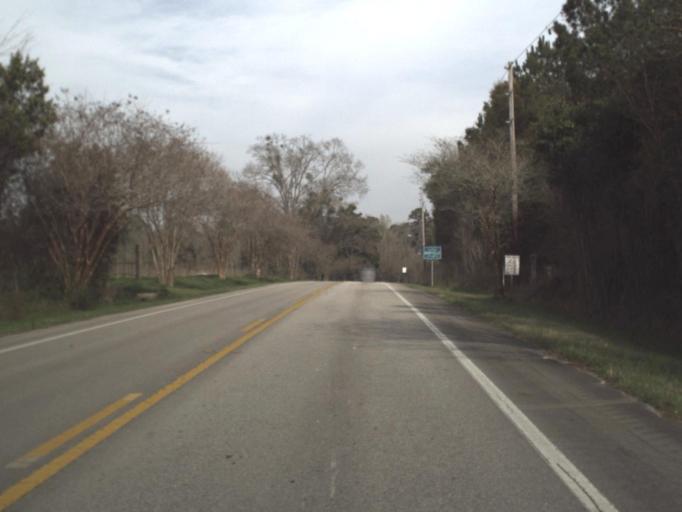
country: US
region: Florida
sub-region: Jefferson County
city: Monticello
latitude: 30.5445
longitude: -83.8941
